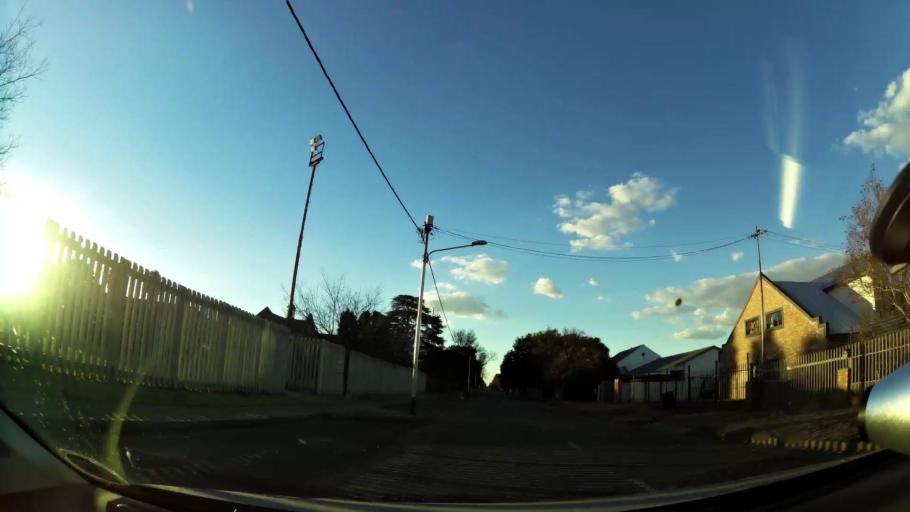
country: ZA
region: North-West
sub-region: Dr Kenneth Kaunda District Municipality
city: Potchefstroom
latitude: -26.7258
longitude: 27.0920
